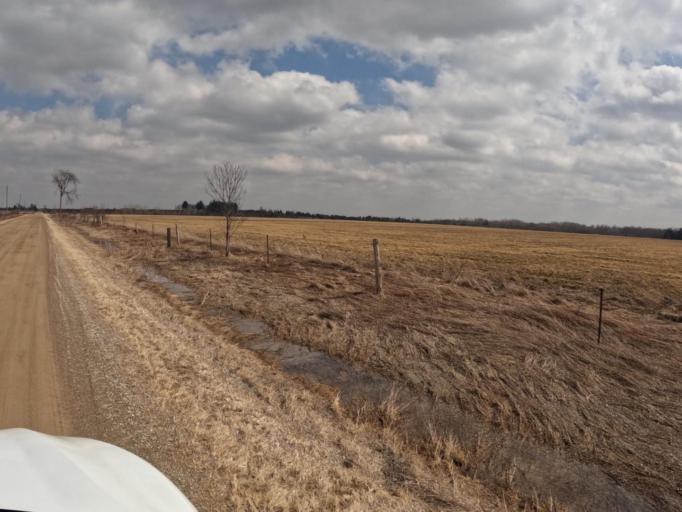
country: CA
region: Ontario
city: Shelburne
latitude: 44.0145
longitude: -80.3268
